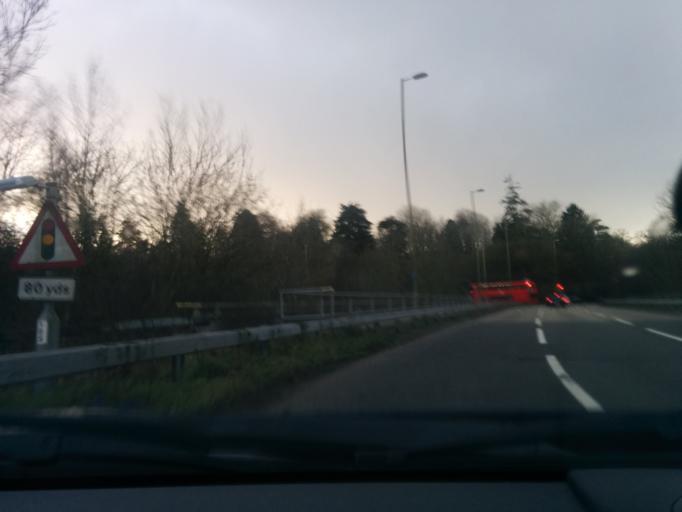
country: GB
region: England
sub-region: Oxfordshire
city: Oxford
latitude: 51.7276
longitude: -1.2578
